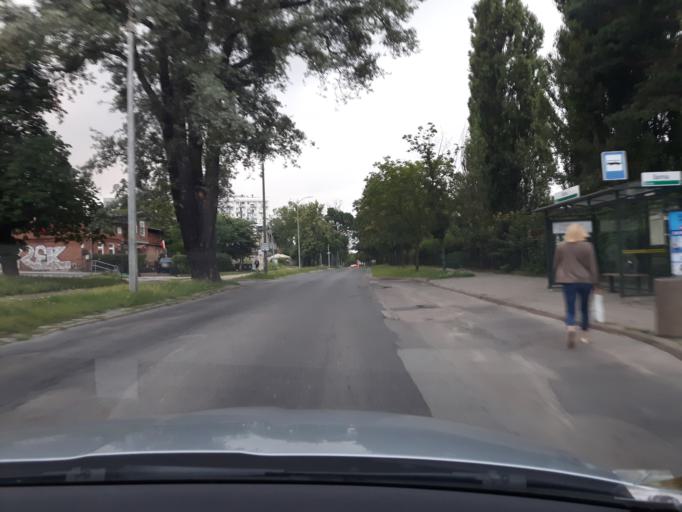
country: PL
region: Pomeranian Voivodeship
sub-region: Sopot
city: Sopot
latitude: 54.4161
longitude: 18.5585
